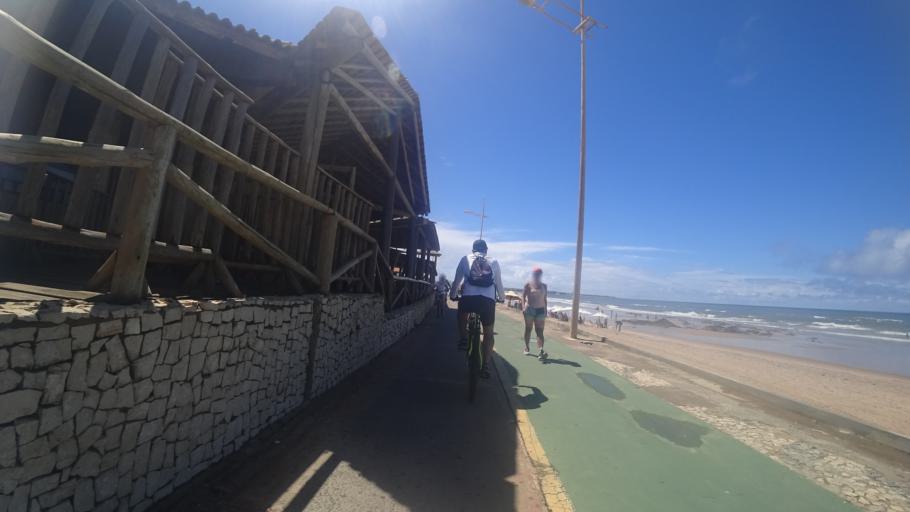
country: BR
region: Bahia
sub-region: Lauro De Freitas
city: Lauro de Freitas
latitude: -12.9664
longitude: -38.4038
